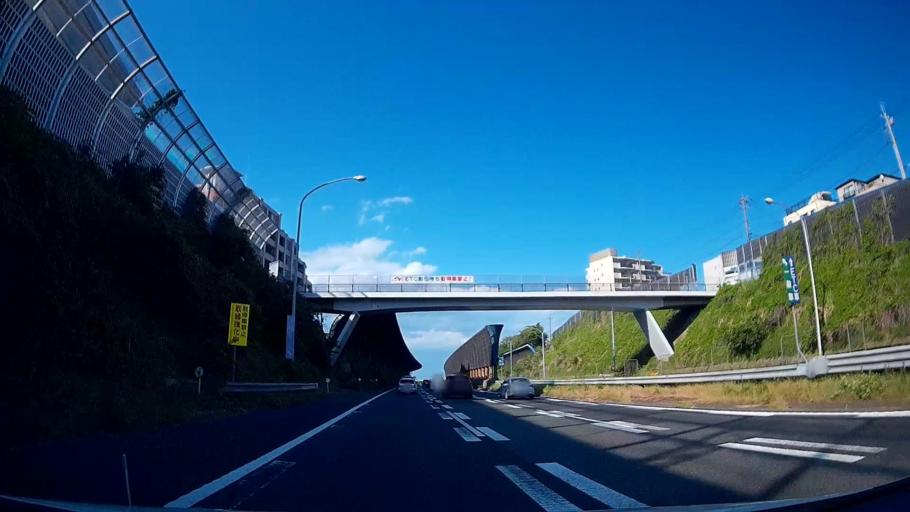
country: JP
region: Tokyo
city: Chofugaoka
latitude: 35.5905
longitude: 139.5695
